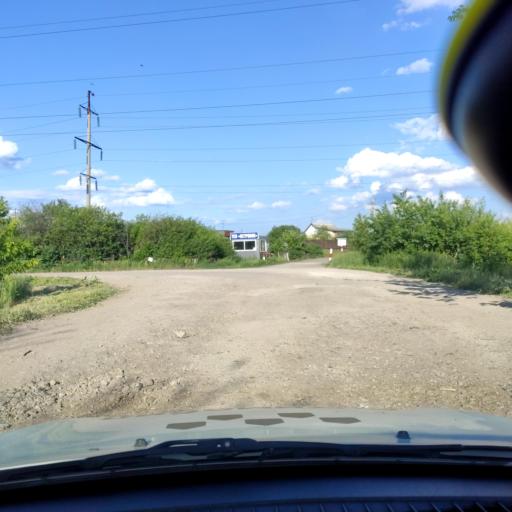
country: RU
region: Samara
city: Tol'yatti
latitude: 53.5868
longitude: 49.4346
